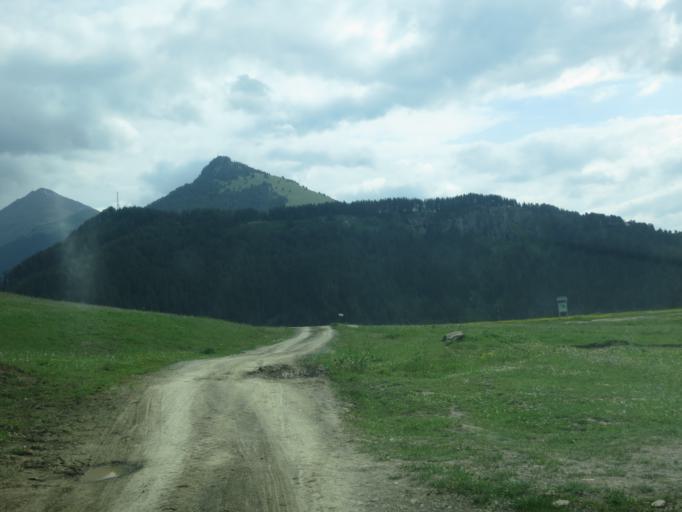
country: RU
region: Chechnya
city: Itum-Kali
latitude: 42.3682
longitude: 45.6358
